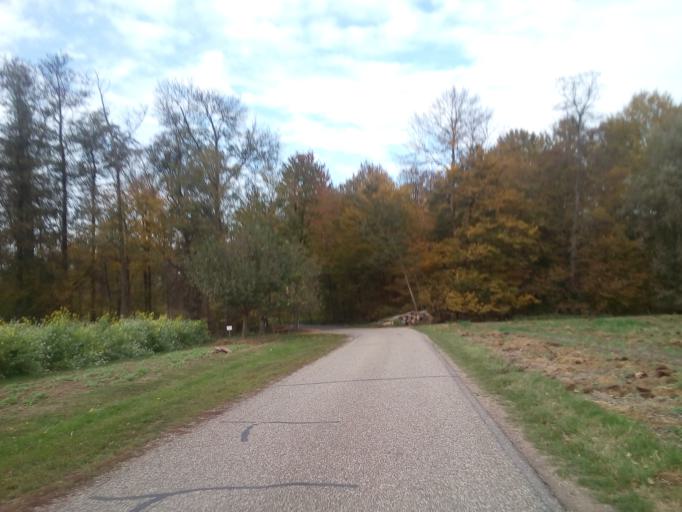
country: DE
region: Baden-Wuerttemberg
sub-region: Karlsruhe Region
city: Zell
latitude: 48.6859
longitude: 8.0460
